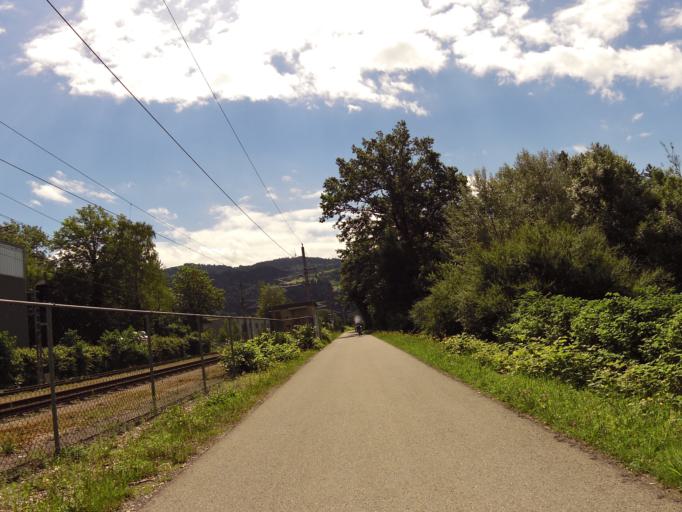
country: AT
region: Vorarlberg
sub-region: Politischer Bezirk Bregenz
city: Lochau
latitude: 47.5326
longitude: 9.7383
